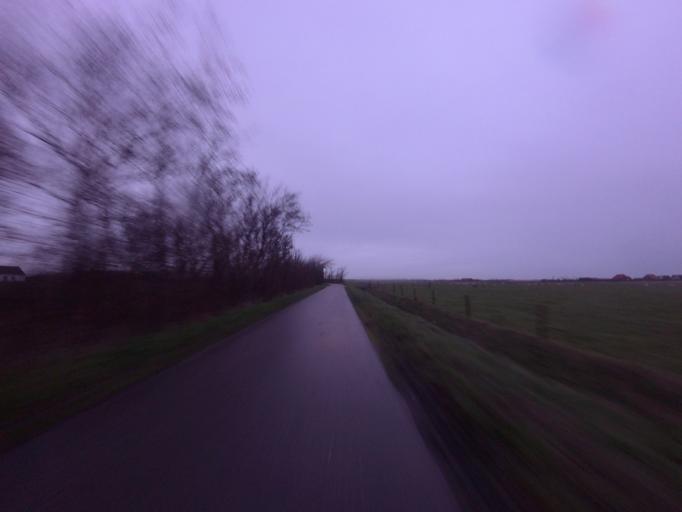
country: NL
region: North Holland
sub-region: Gemeente Texel
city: Den Burg
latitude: 53.0663
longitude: 4.8012
